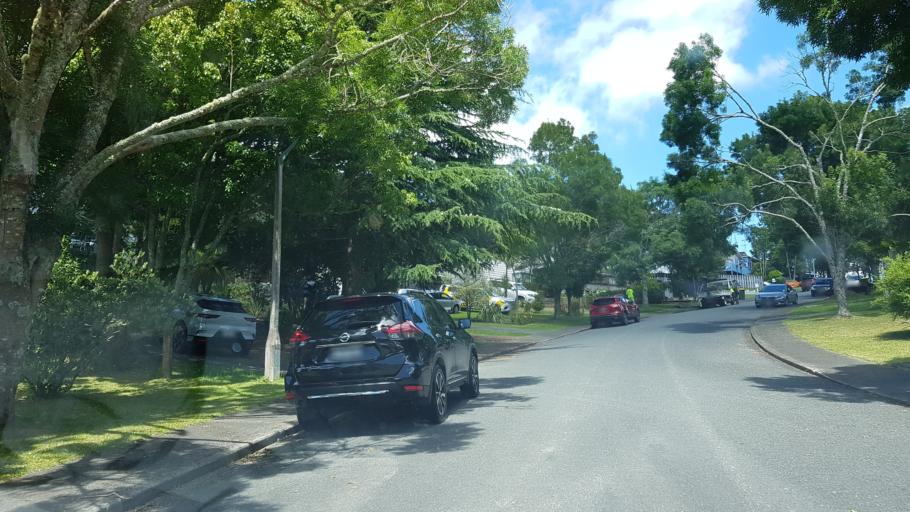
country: NZ
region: Auckland
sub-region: Auckland
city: North Shore
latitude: -36.7874
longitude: 174.7140
